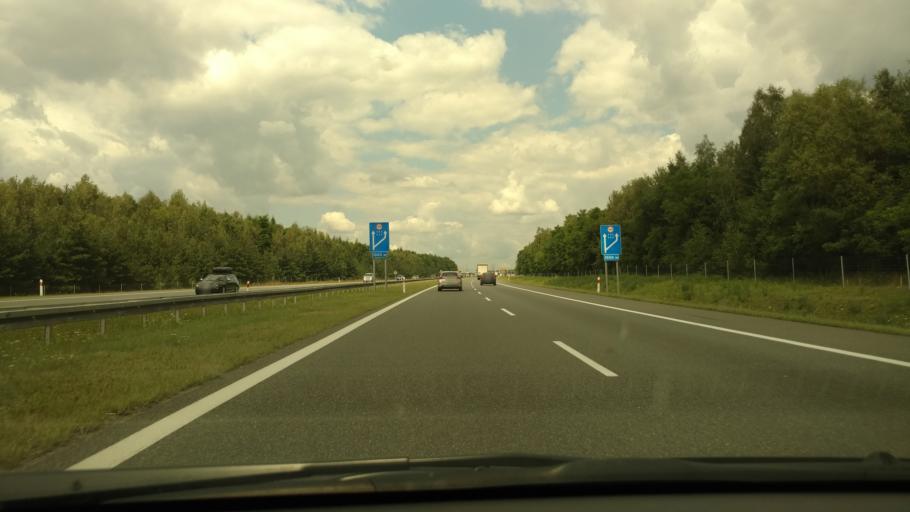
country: PL
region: Silesian Voivodeship
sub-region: Myslowice
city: Myslowice
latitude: 50.1875
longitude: 19.1911
